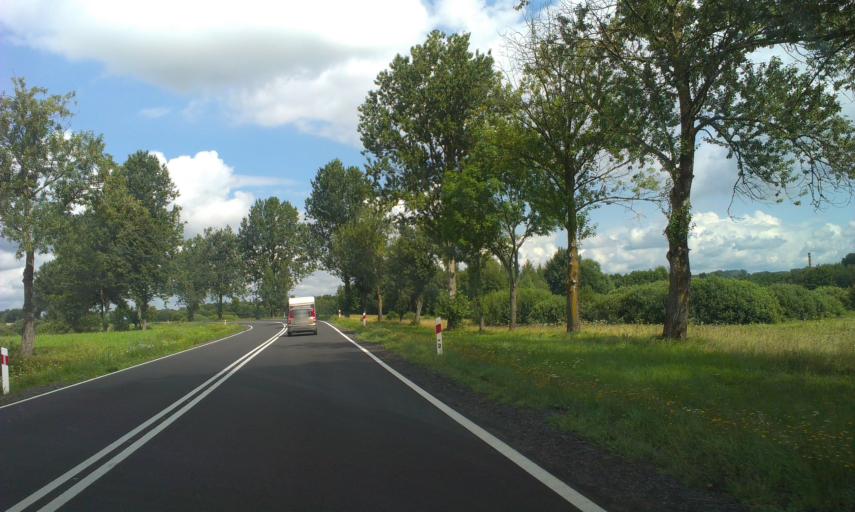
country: PL
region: West Pomeranian Voivodeship
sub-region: Powiat koszalinski
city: Bobolice
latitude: 53.9418
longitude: 16.5906
